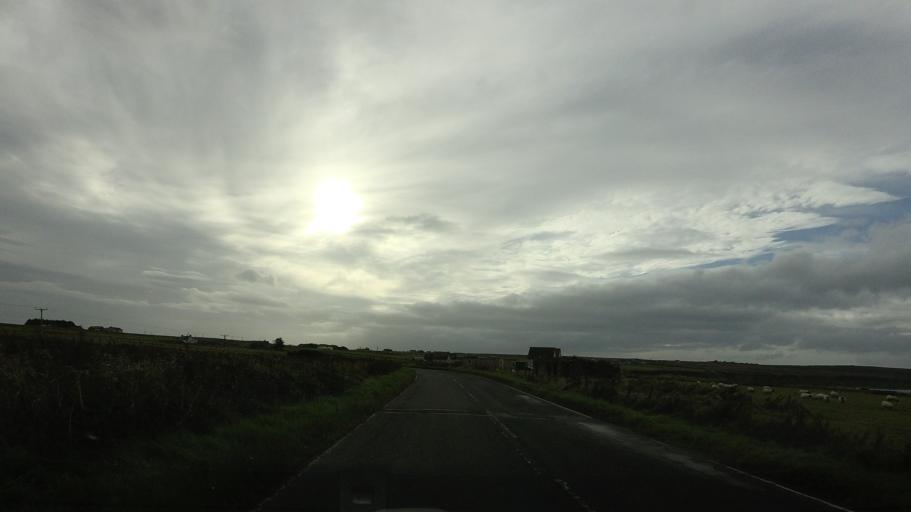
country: GB
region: Scotland
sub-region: Highland
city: Wick
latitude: 58.6370
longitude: -3.1500
